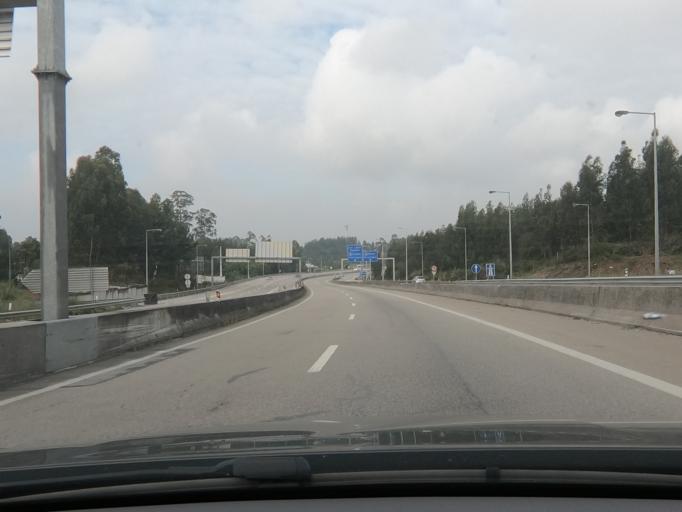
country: PT
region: Porto
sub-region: Vila Nova de Gaia
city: Grijo
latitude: 41.0118
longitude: -8.5749
